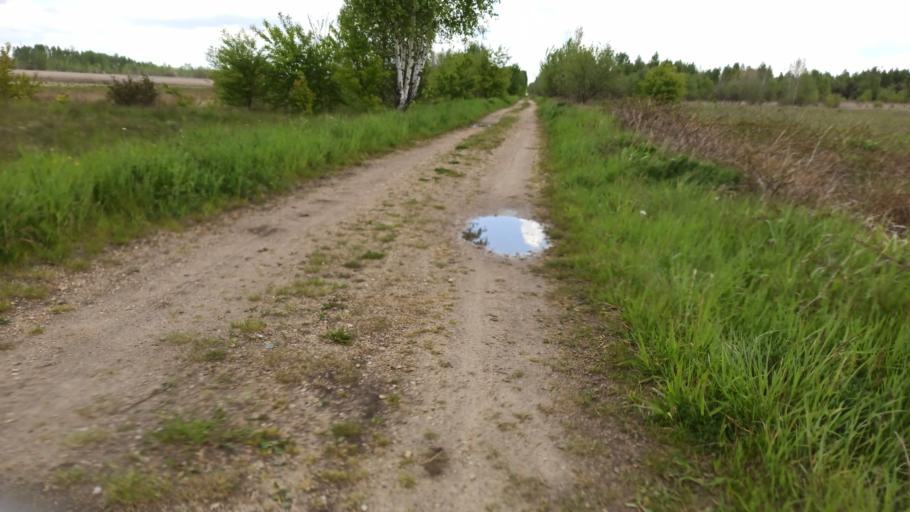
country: PL
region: Swietokrzyskie
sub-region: Powiat skarzyski
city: Skarzysko Koscielne
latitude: 51.1408
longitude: 20.9033
